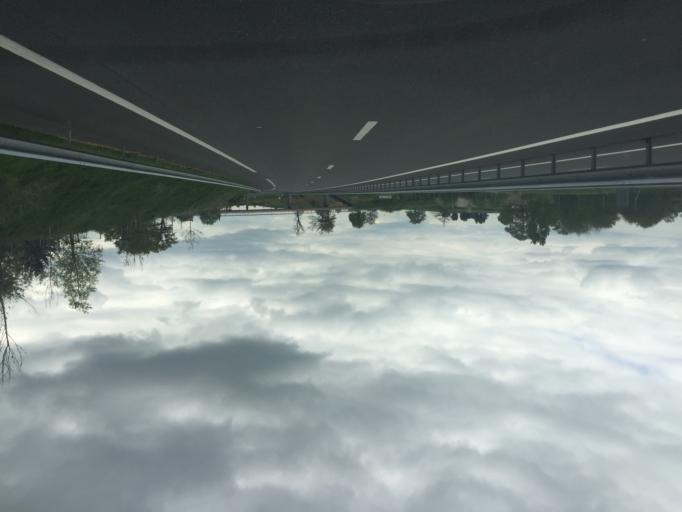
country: FR
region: Rhone-Alpes
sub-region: Departement de la Loire
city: La Pacaudiere
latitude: 46.1802
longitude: 3.8777
